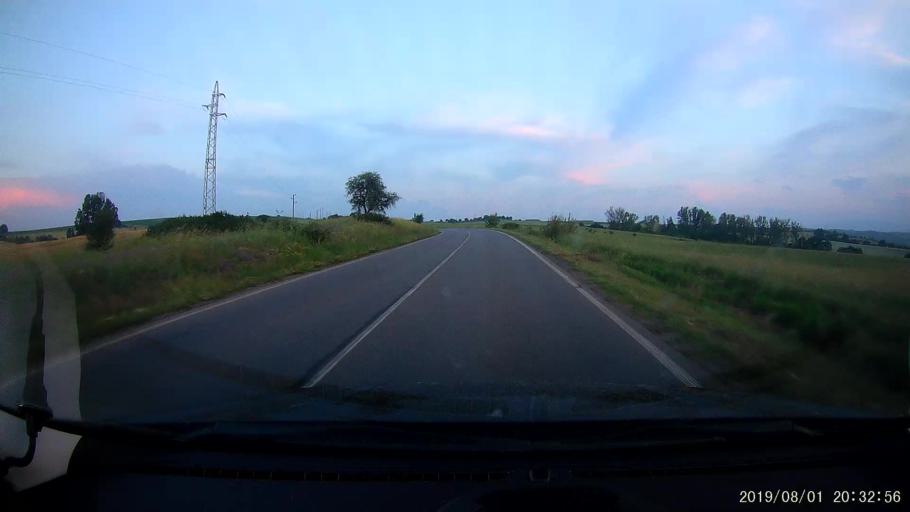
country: BG
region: Yambol
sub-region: Obshtina Elkhovo
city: Elkhovo
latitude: 42.1142
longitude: 26.5310
